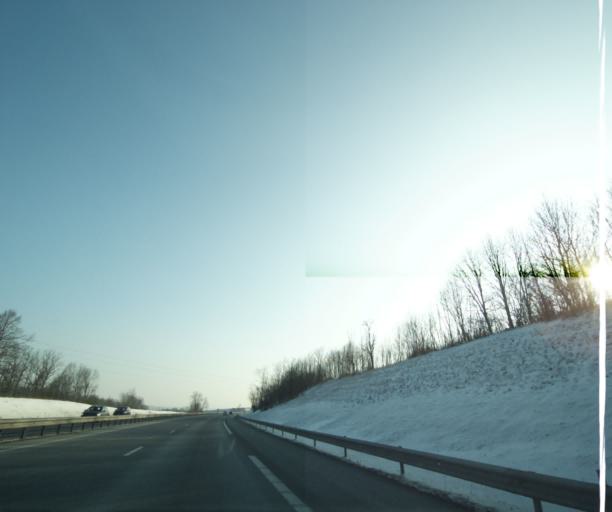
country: FR
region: Rhone-Alpes
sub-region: Departement de l'Ain
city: Chatillon-en-Michaille
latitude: 46.1348
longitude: 5.7976
